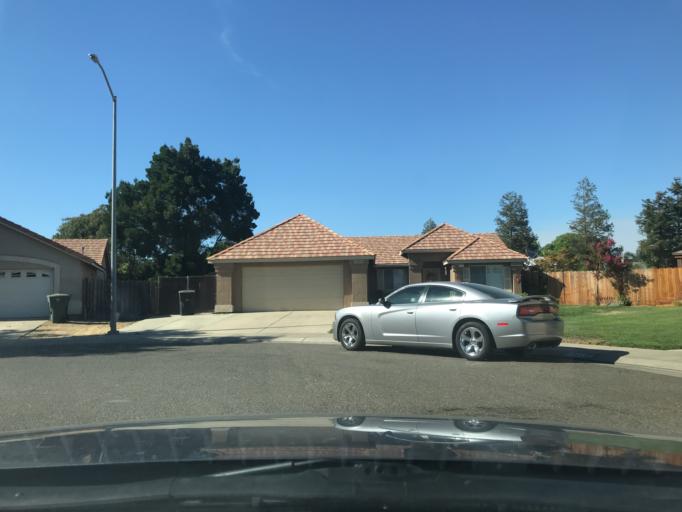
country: US
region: California
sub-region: Merced County
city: Atwater
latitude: 37.3492
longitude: -120.5837
